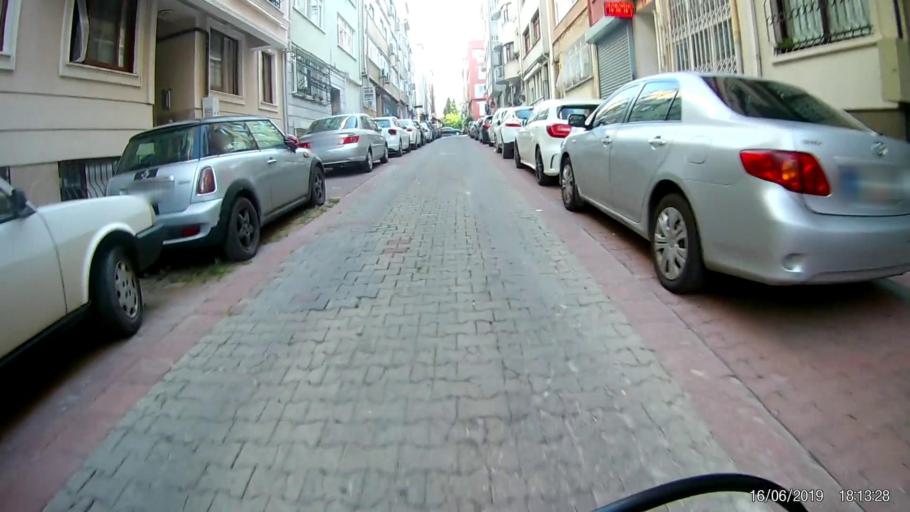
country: TR
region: Istanbul
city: UEskuedar
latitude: 40.9849
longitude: 29.0302
